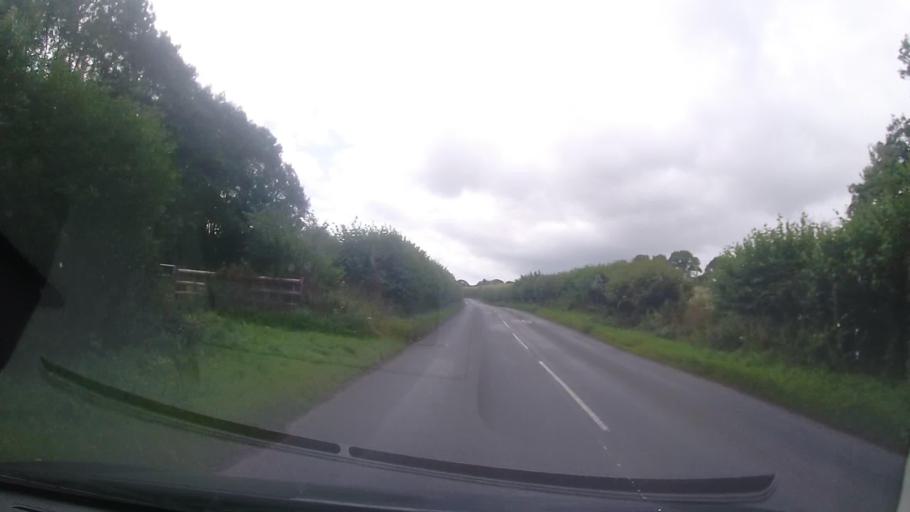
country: GB
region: England
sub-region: Shropshire
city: Craven Arms
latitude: 52.4385
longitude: -2.8608
